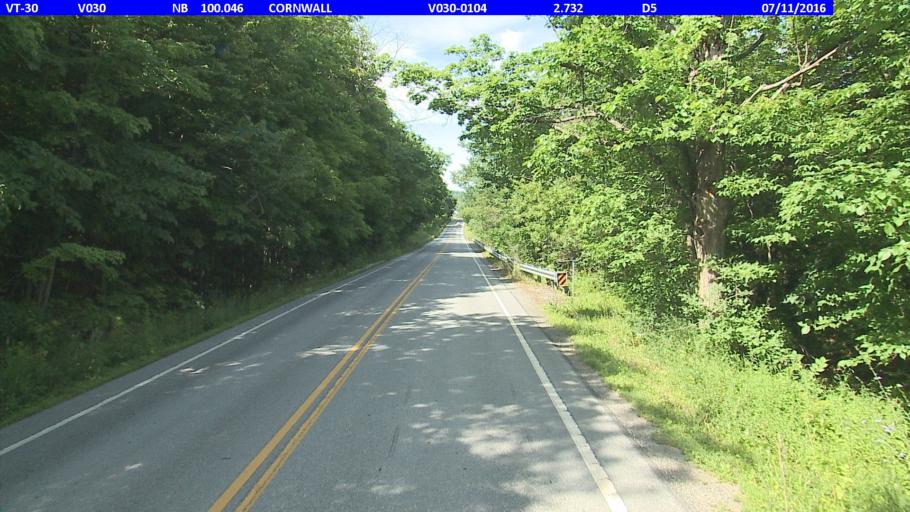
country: US
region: Vermont
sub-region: Addison County
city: Middlebury (village)
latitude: 43.9471
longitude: -73.2109
